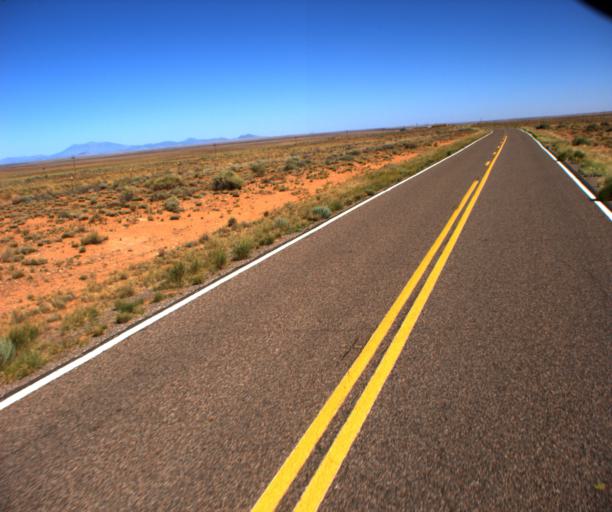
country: US
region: Arizona
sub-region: Coconino County
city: LeChee
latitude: 35.1091
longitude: -110.8663
